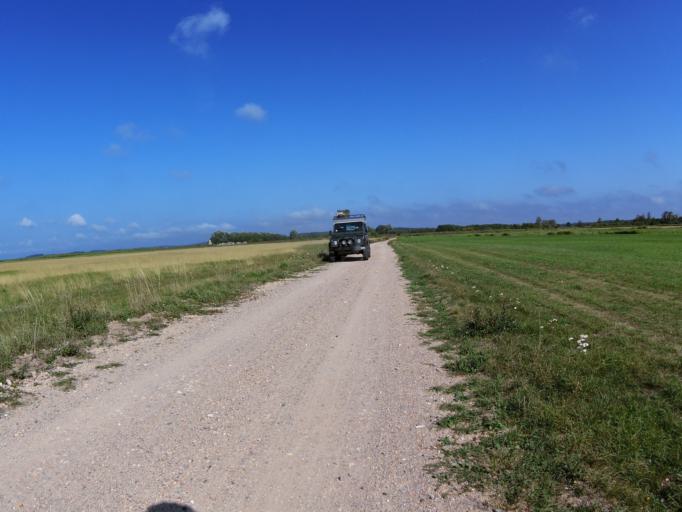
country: DE
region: Mecklenburg-Vorpommern
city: Loddin
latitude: 53.9759
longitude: 14.0513
